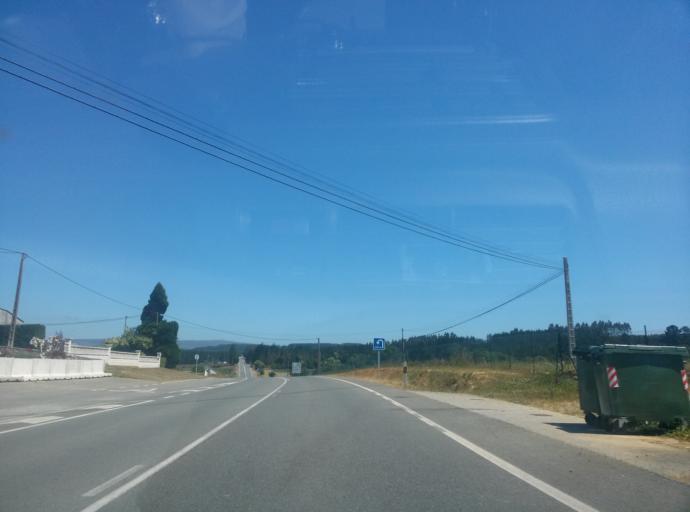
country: ES
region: Galicia
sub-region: Provincia de Lugo
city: Castro de Rei
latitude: 43.2355
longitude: -7.3992
